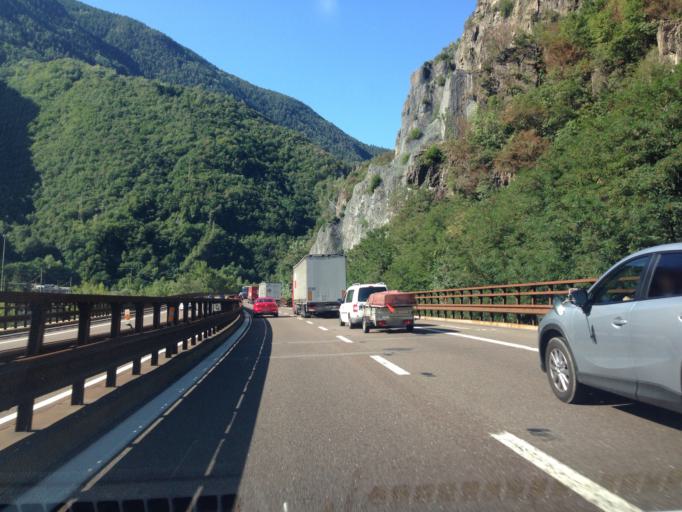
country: IT
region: Trentino-Alto Adige
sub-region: Bolzano
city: Cornedo All'Isarco
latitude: 46.4954
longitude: 11.4413
